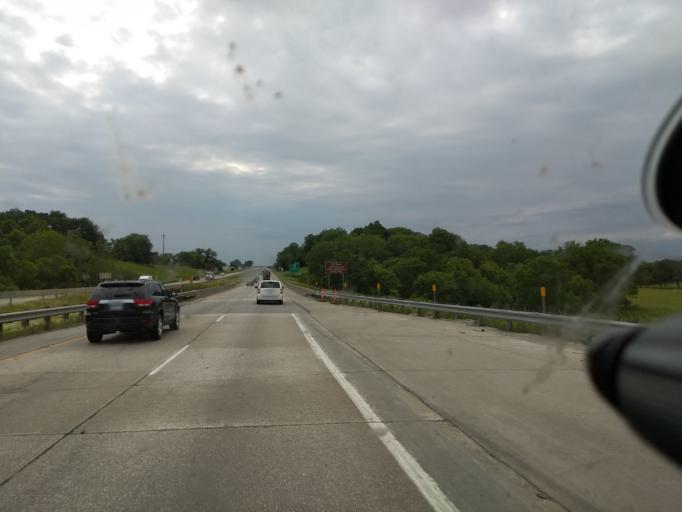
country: US
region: Iowa
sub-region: Dallas County
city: Waukee
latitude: 41.5656
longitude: -93.8630
